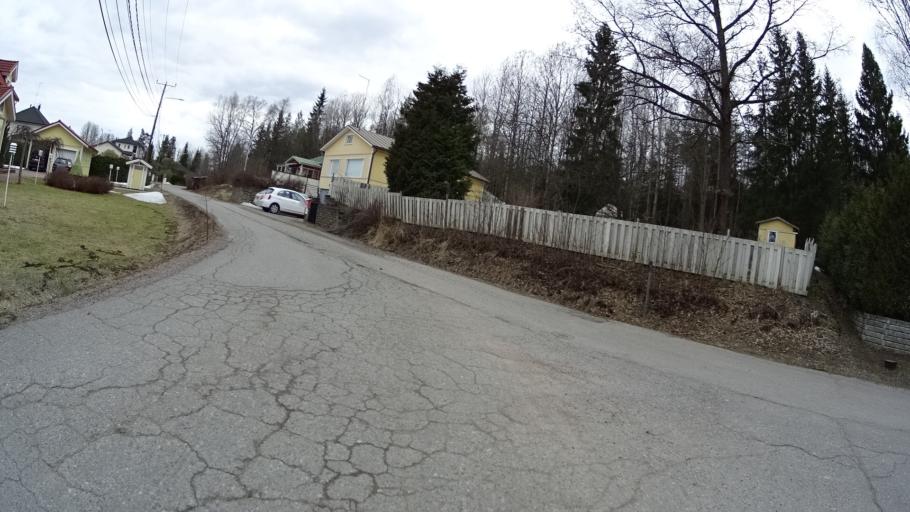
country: FI
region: Uusimaa
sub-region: Helsinki
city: Kilo
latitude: 60.2982
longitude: 24.7864
